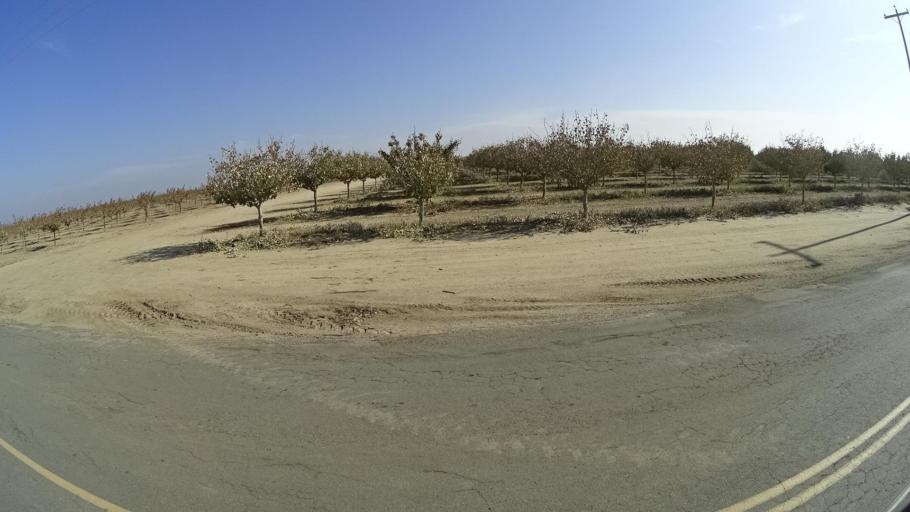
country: US
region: California
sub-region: Kern County
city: McFarland
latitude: 35.6129
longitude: -119.1688
